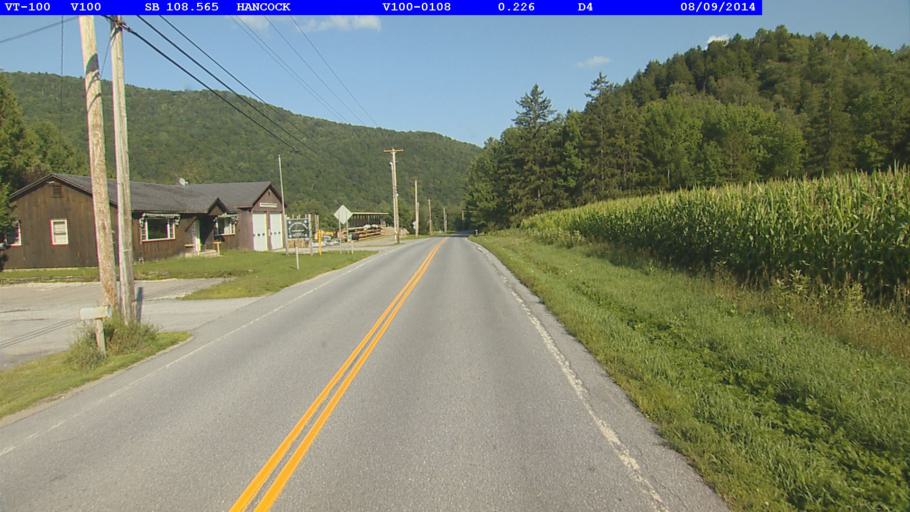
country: US
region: Vermont
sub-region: Orange County
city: Randolph
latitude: 43.9137
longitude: -72.8370
